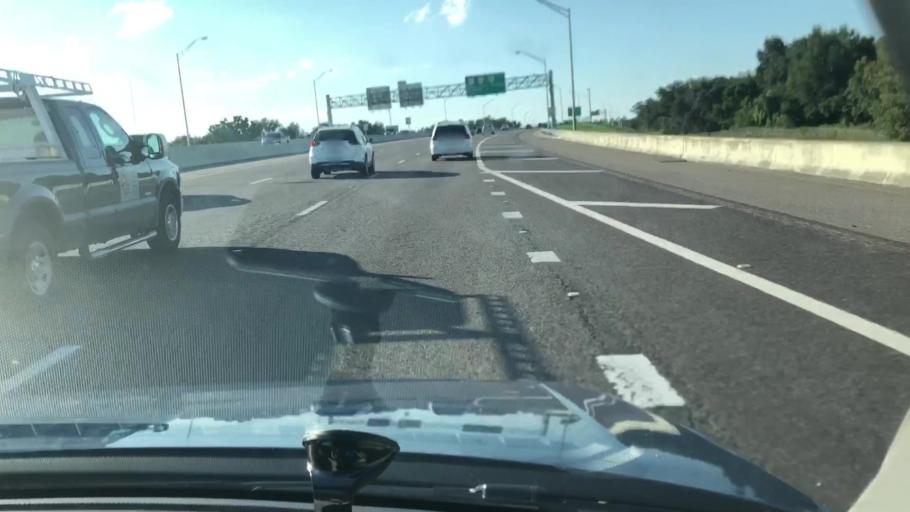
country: US
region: Florida
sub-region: Orange County
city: South Apopka
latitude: 28.6469
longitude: -81.5143
